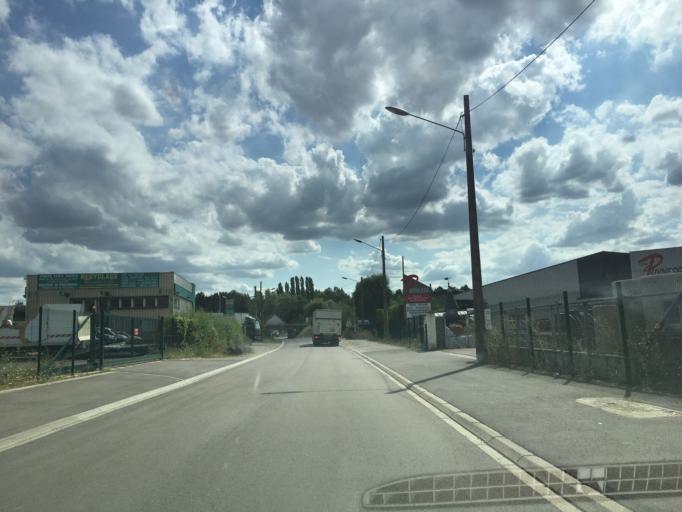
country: FR
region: Bourgogne
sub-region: Departement de l'Yonne
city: Joigny
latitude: 47.9741
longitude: 3.3852
